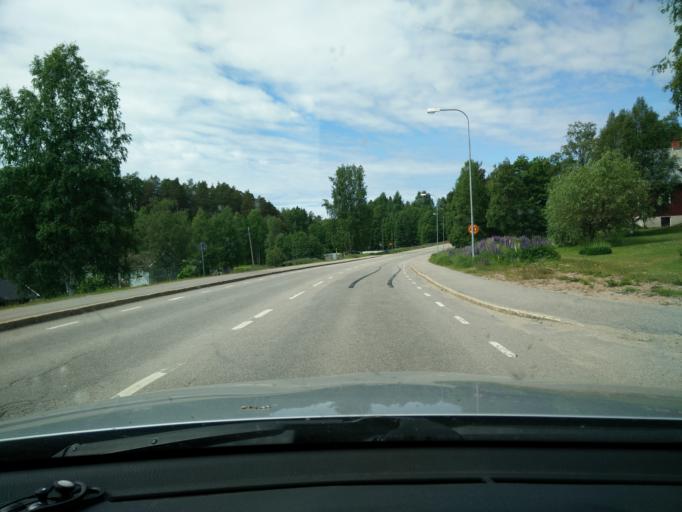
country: SE
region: Gaevleborg
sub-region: Hudiksvalls Kommun
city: Delsbo
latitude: 62.1103
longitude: 16.7028
